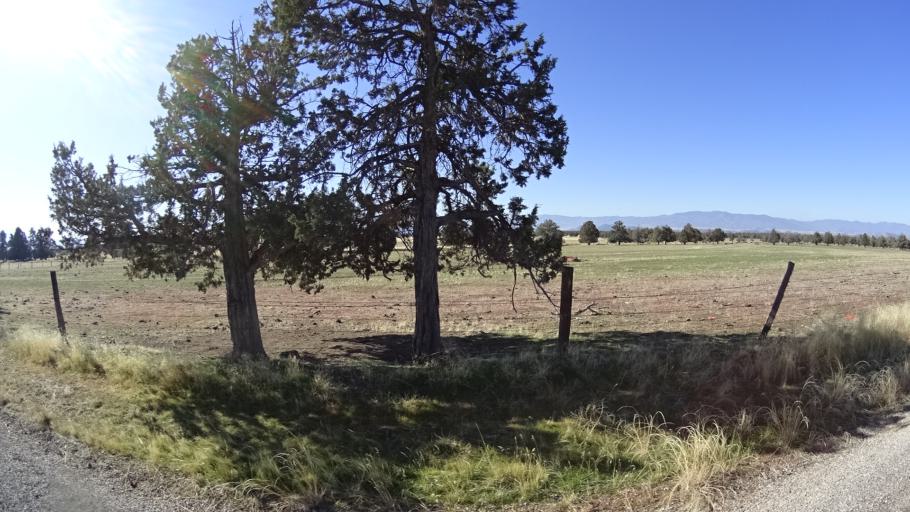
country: US
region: California
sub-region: Siskiyou County
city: Weed
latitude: 41.6257
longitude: -122.3291
